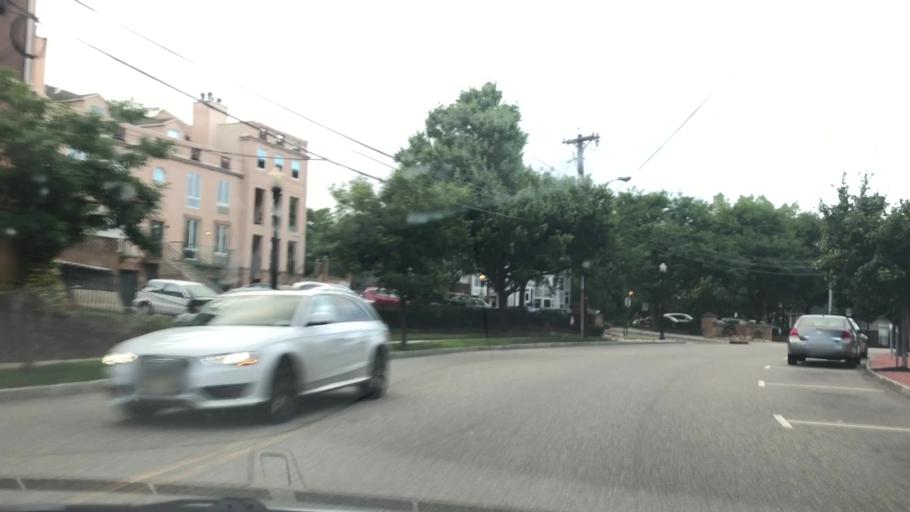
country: US
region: New Jersey
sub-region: Essex County
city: Glen Ridge
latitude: 40.8087
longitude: -74.2100
